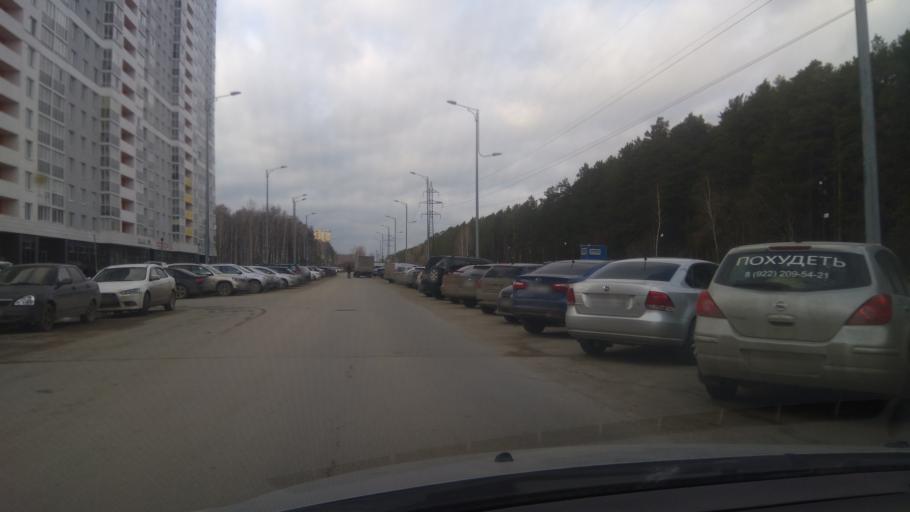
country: RU
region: Sverdlovsk
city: Sovkhoznyy
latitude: 56.7857
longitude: 60.5494
